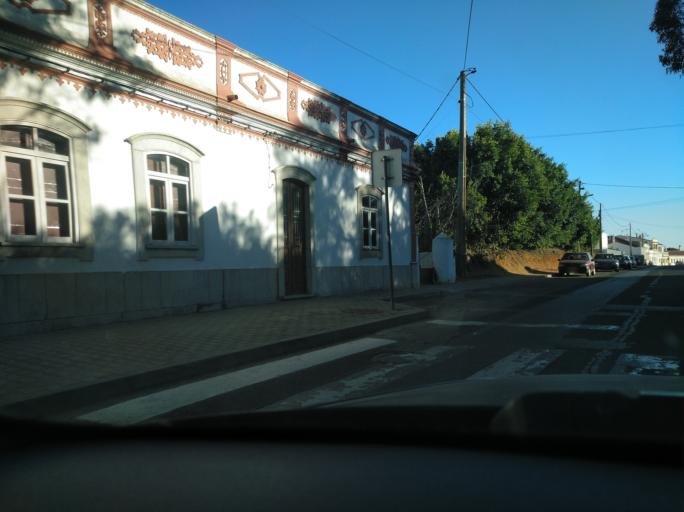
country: PT
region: Faro
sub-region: Vila Real de Santo Antonio
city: Monte Gordo
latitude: 37.1735
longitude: -7.5353
